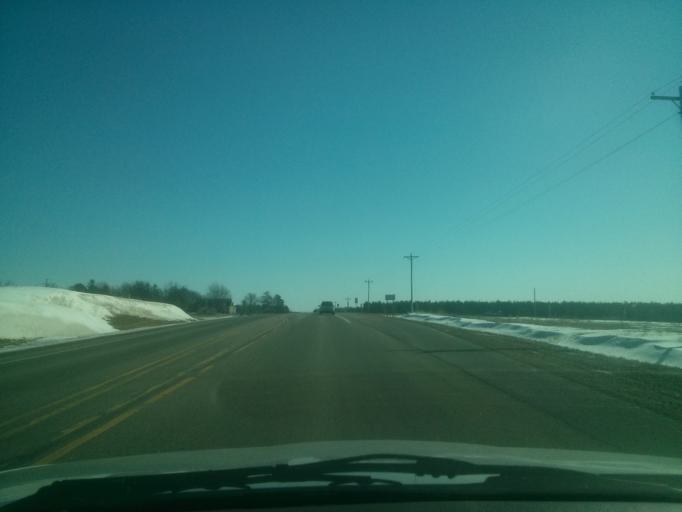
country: US
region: Wisconsin
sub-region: Saint Croix County
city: New Richmond
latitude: 45.1368
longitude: -92.4384
